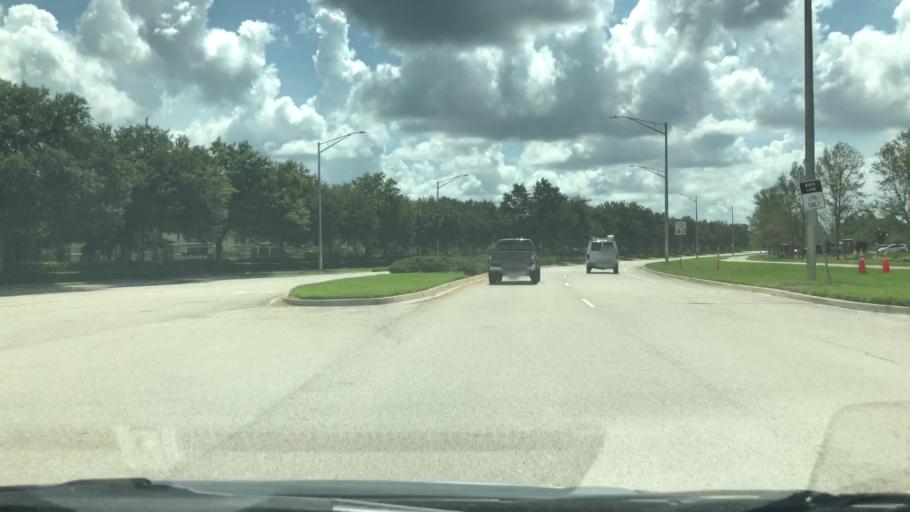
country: US
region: Florida
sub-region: Saint Johns County
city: Fruit Cove
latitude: 30.1218
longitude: -81.5255
